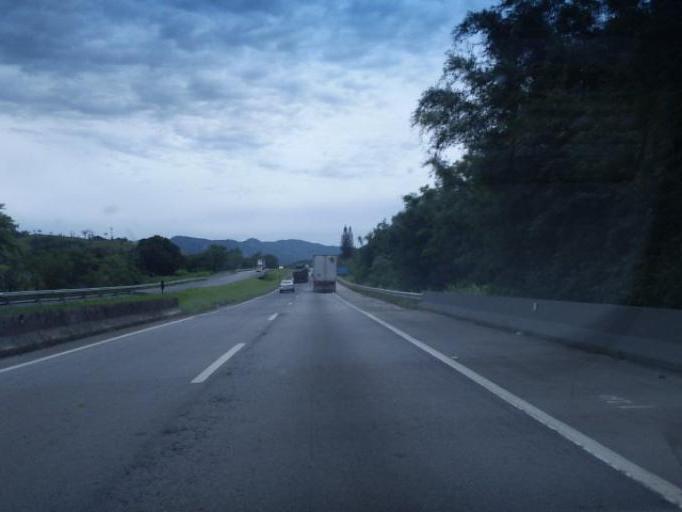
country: BR
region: Sao Paulo
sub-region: Miracatu
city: Miracatu
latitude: -24.2439
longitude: -47.3660
